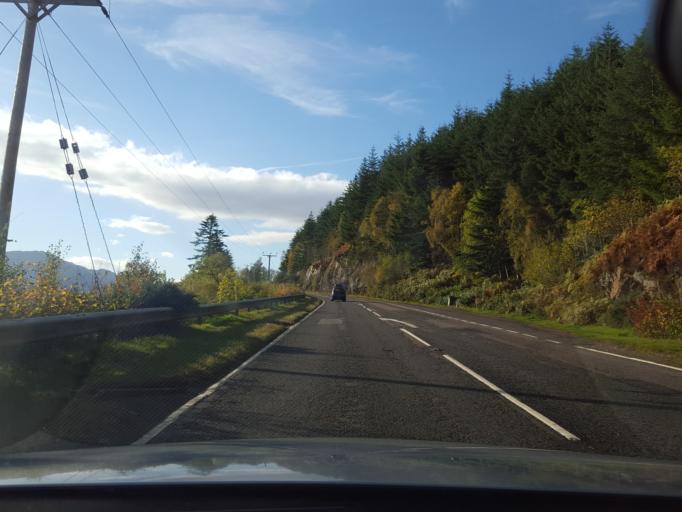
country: GB
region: Scotland
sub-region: Highland
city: Beauly
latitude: 57.2264
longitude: -4.5718
